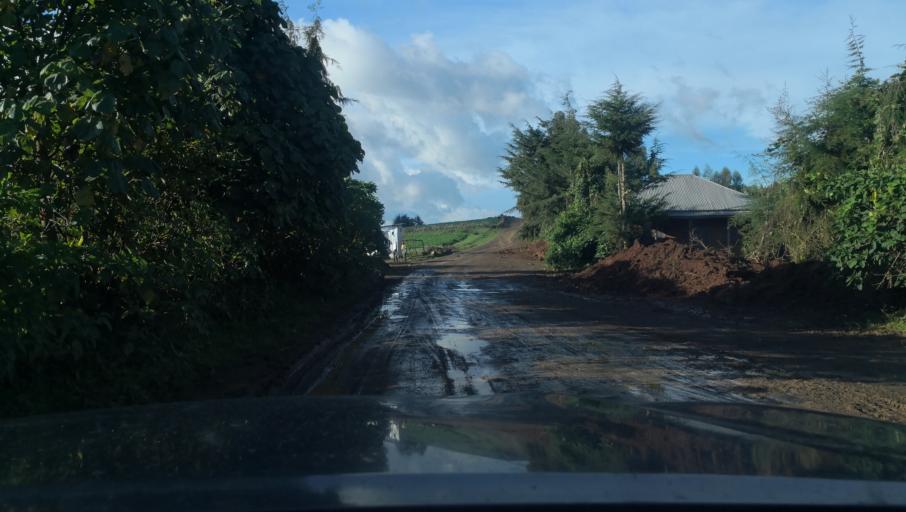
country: ET
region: Southern Nations, Nationalities, and People's Region
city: Butajira
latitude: 8.3943
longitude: 38.3119
